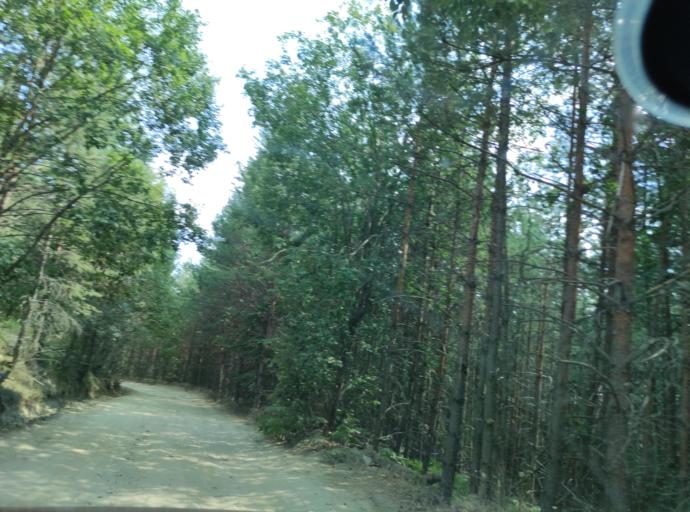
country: BG
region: Blagoevgrad
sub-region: Obshtina Belitsa
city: Belitsa
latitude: 42.0258
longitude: 23.5791
